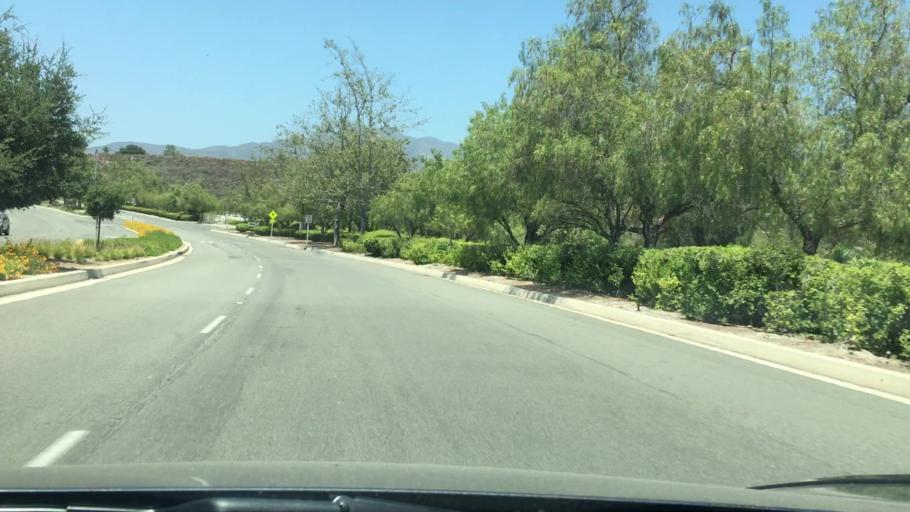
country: US
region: California
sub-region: Orange County
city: Rancho Santa Margarita
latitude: 33.6344
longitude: -117.5862
